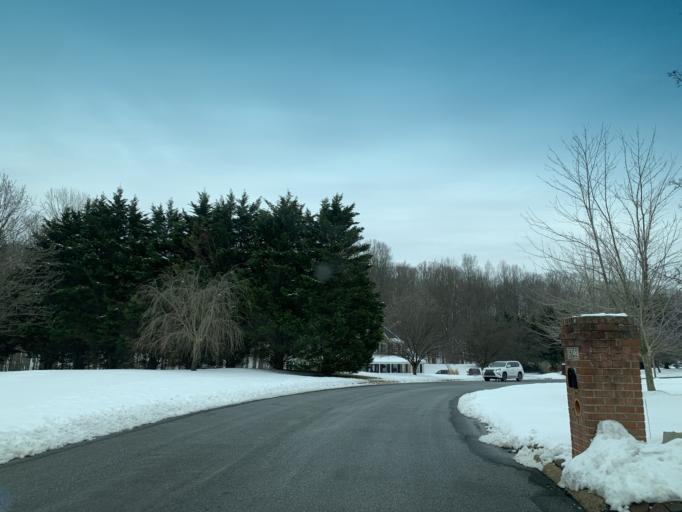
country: US
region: Maryland
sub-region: Harford County
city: Jarrettsville
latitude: 39.5836
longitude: -76.4629
